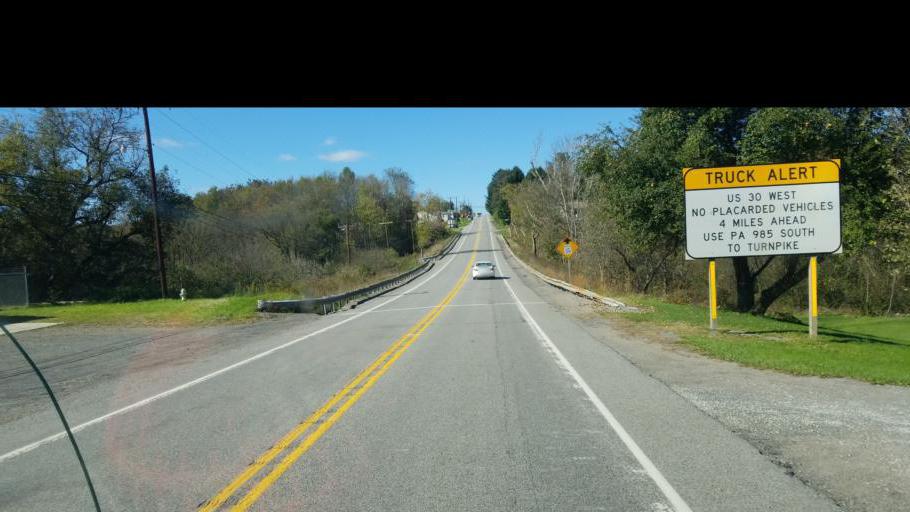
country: US
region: Pennsylvania
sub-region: Somerset County
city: Boswell
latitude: 40.1567
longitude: -79.0581
